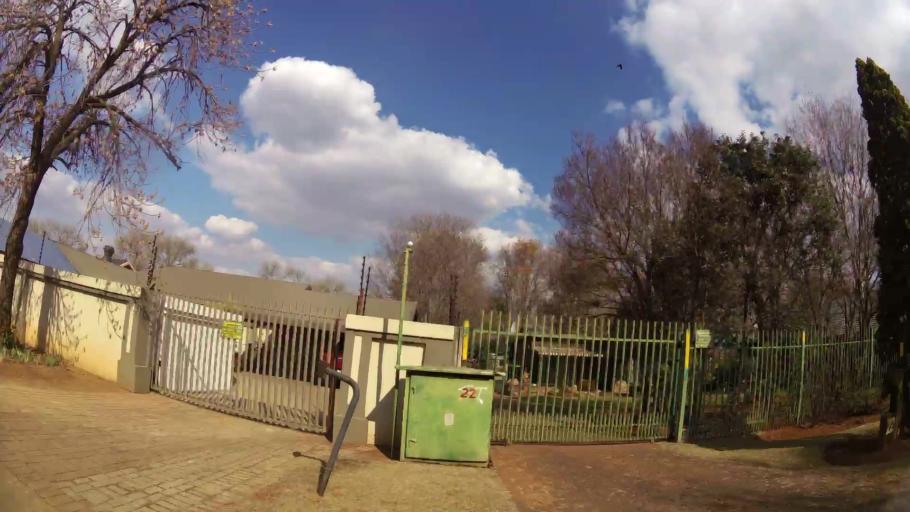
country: ZA
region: Mpumalanga
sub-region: Nkangala District Municipality
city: Delmas
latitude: -26.1425
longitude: 28.6738
